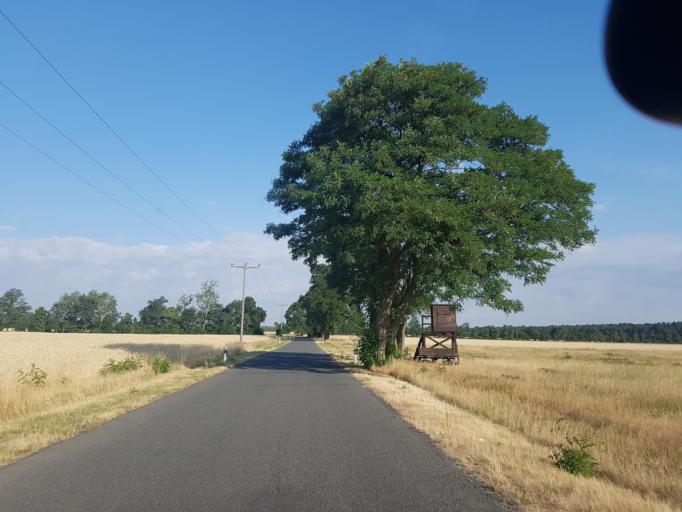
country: DE
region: Saxony-Anhalt
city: Seyda
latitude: 51.9198
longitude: 12.9428
